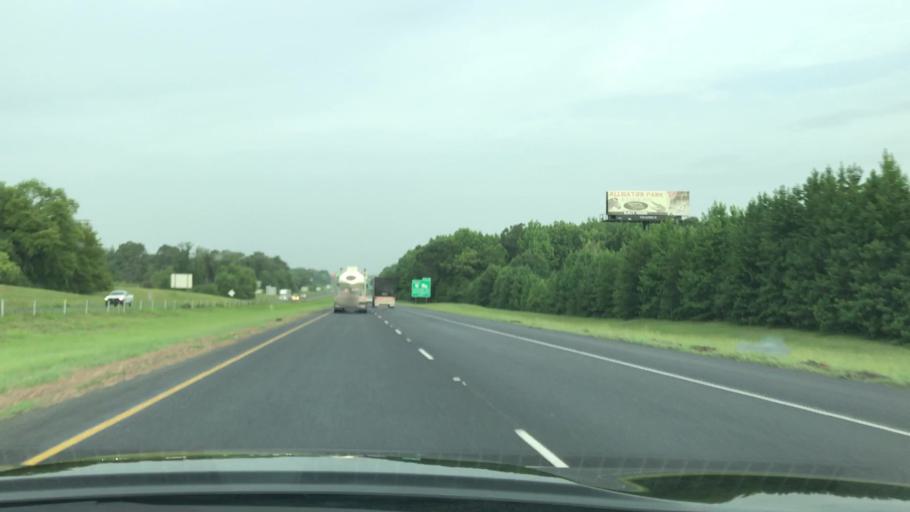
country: US
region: Louisiana
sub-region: Caddo Parish
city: Greenwood
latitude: 32.4450
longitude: -93.9583
